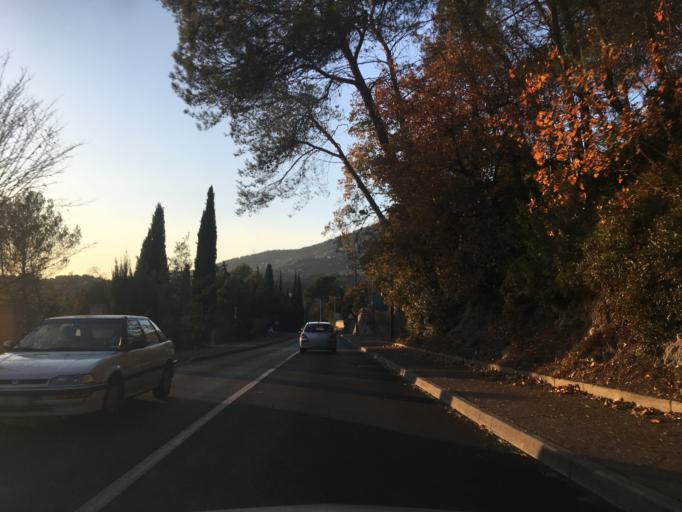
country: FR
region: Provence-Alpes-Cote d'Azur
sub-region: Departement des Alpes-Maritimes
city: Peymeinade
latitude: 43.6389
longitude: 6.8749
